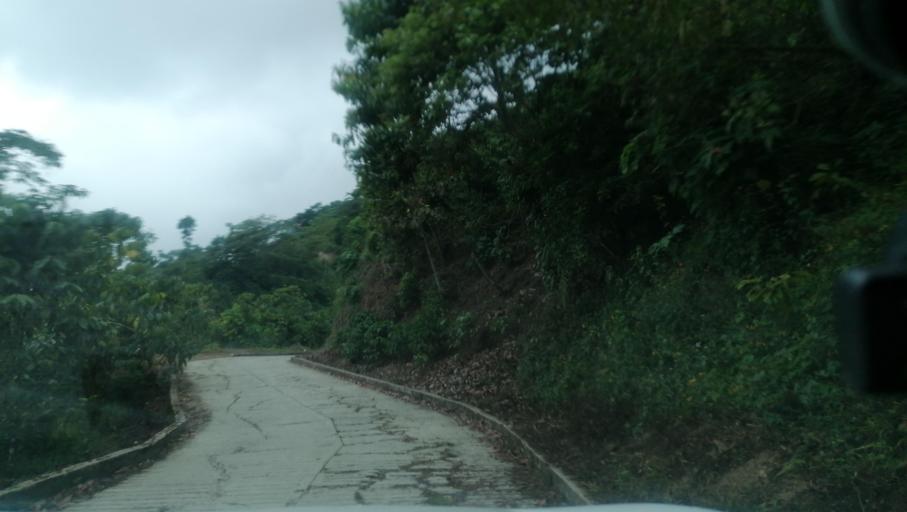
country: MX
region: Chiapas
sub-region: Cacahoatan
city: Benito Juarez
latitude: 15.0875
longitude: -92.1604
